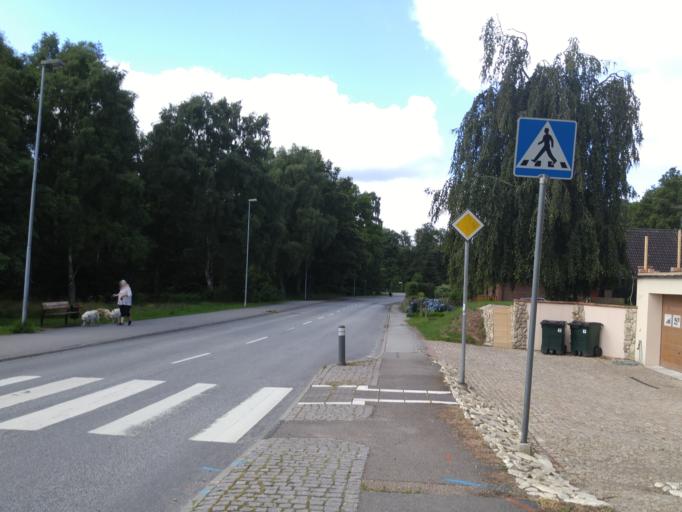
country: SE
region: Skane
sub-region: Hoors Kommun
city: Hoeoer
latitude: 55.9272
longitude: 13.5365
